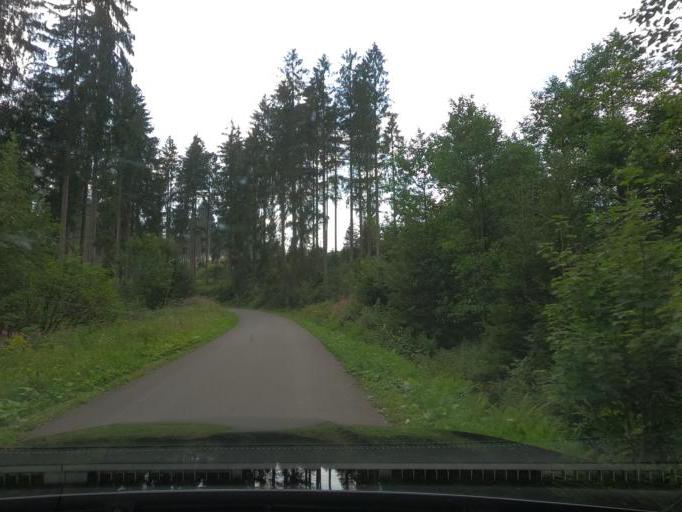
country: DE
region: Lower Saxony
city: Wildemann
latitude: 51.7882
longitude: 10.2982
